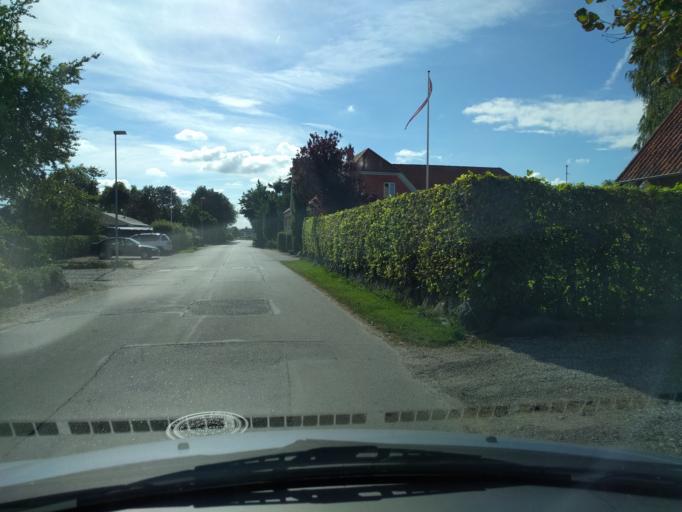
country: DK
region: South Denmark
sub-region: Kerteminde Kommune
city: Munkebo
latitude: 55.4323
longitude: 10.5858
